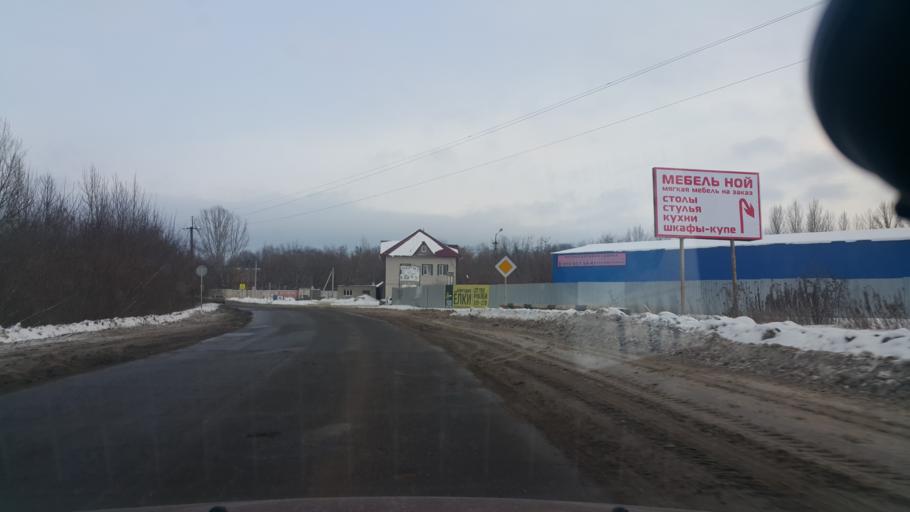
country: RU
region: Tambov
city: Bokino
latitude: 52.6583
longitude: 41.4391
